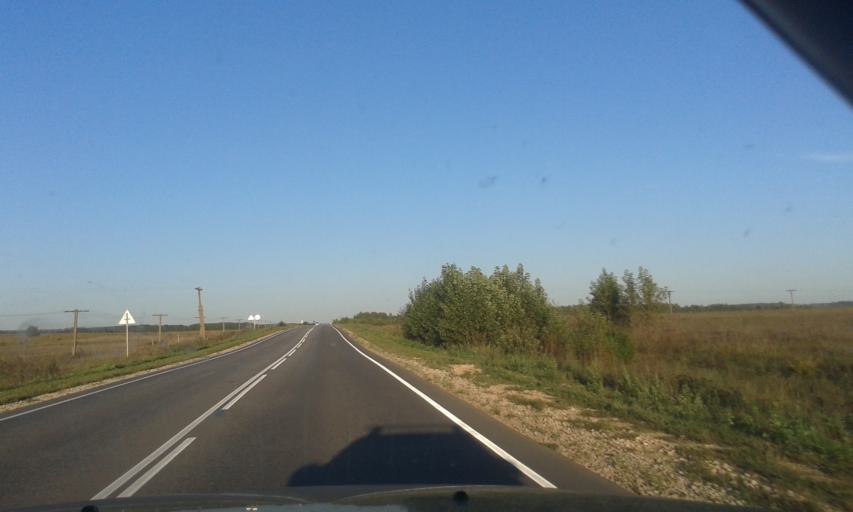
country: RU
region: Tula
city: Krapivna
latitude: 54.1144
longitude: 37.1557
